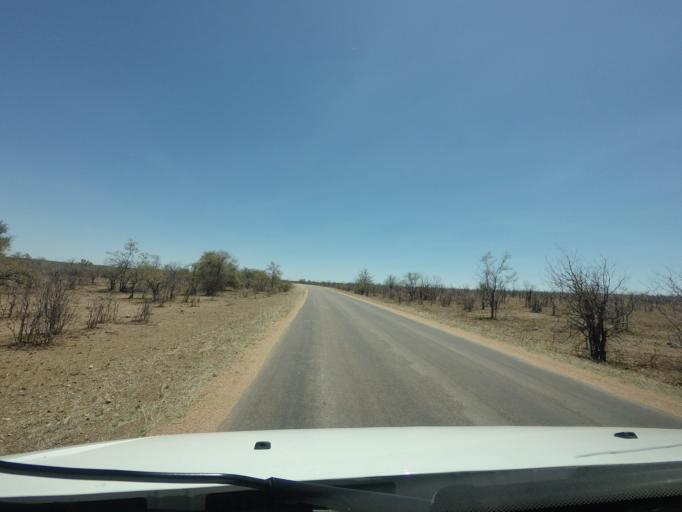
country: ZA
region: Limpopo
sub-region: Mopani District Municipality
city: Phalaborwa
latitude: -23.5945
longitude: 31.4544
